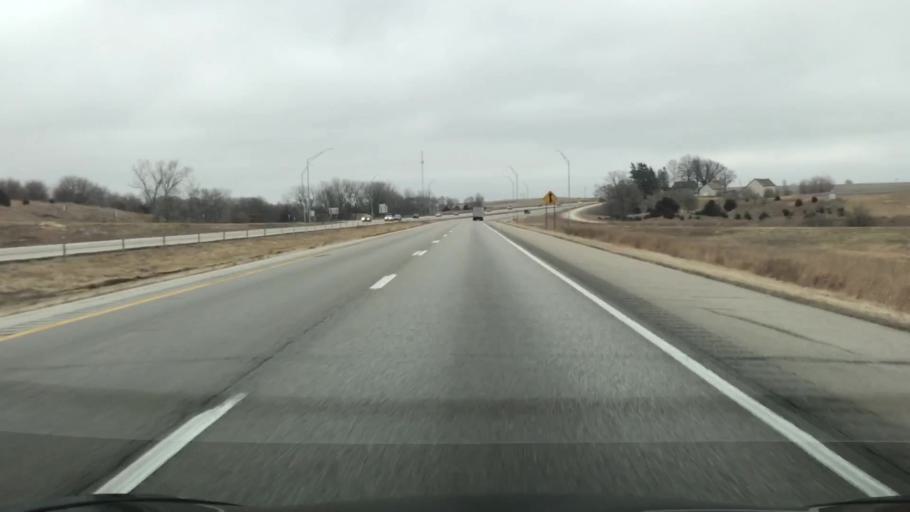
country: US
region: Iowa
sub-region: Madison County
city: Earlham
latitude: 41.5140
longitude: -94.1954
